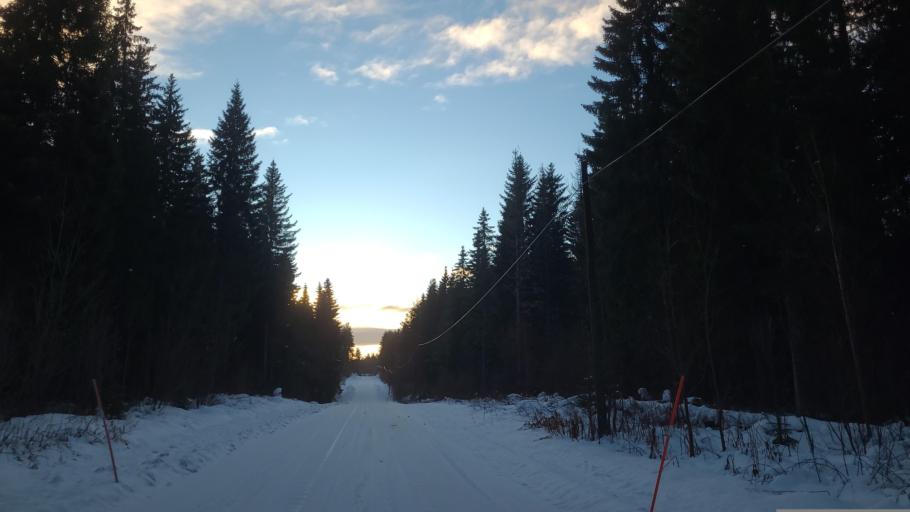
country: SE
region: Gaevleborg
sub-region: Bollnas Kommun
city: Kilafors
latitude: 61.3819
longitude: 16.6854
